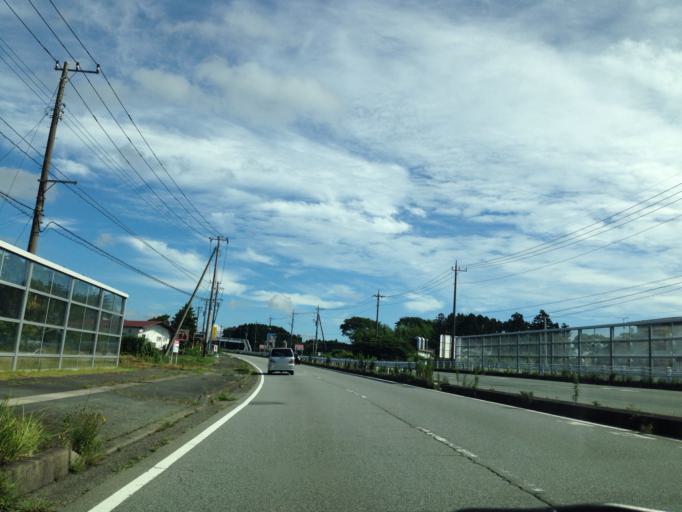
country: JP
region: Shizuoka
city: Gotemba
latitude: 35.2796
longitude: 138.9184
